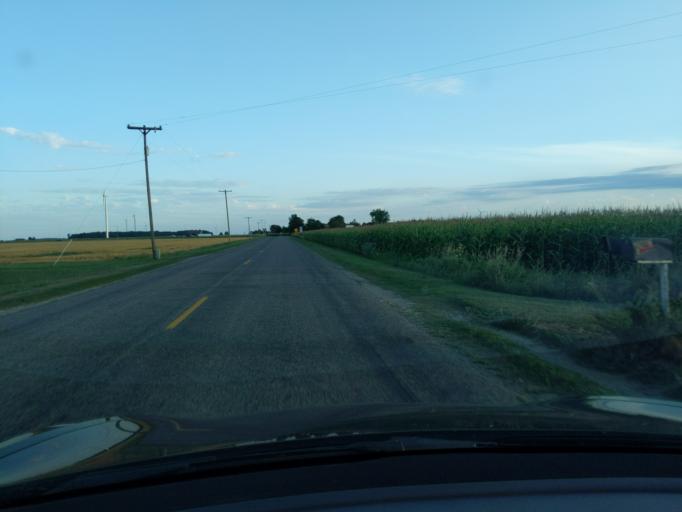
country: US
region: Michigan
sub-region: Gratiot County
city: Saint Louis
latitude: 43.3827
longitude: -84.5480
